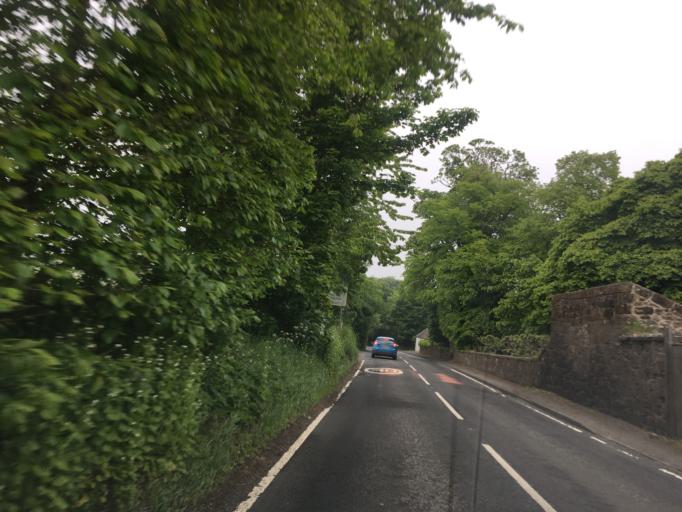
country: GB
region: Scotland
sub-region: Midlothian
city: Penicuik
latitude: 55.8406
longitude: -3.1988
